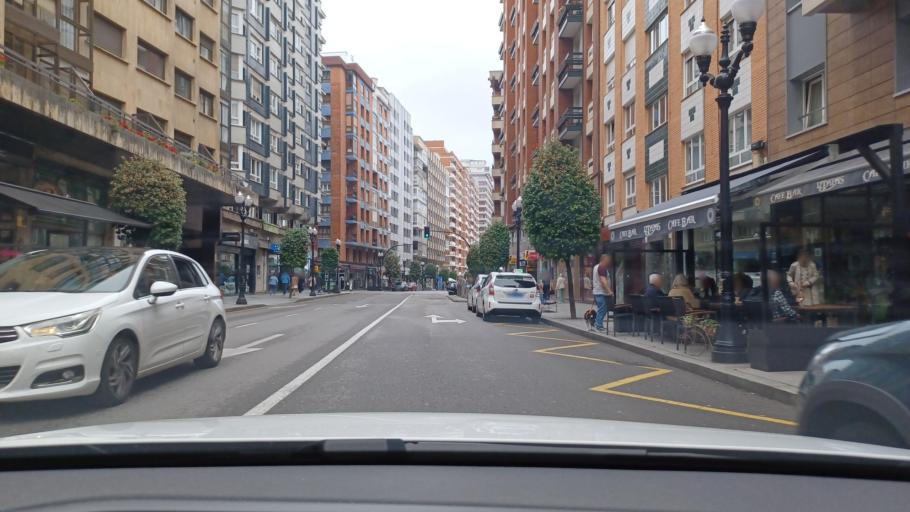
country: ES
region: Asturias
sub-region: Province of Asturias
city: Gijon
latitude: 43.5376
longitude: -5.6529
